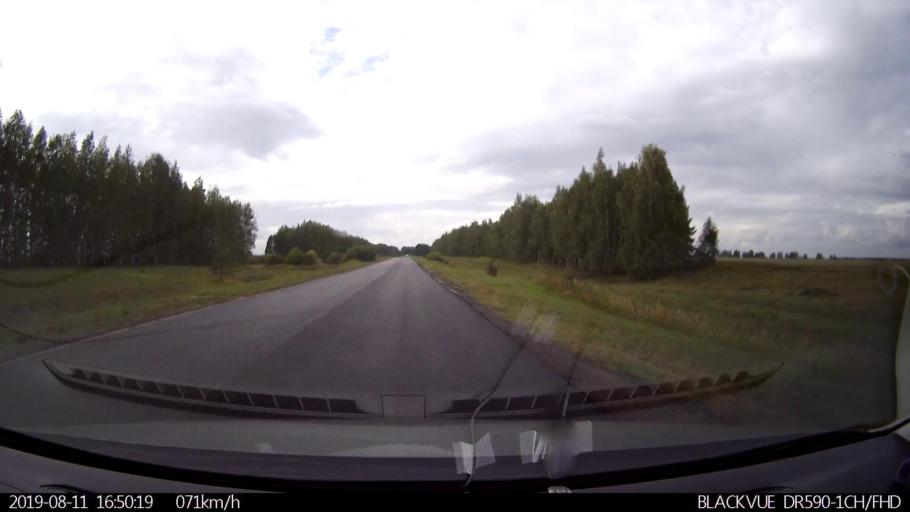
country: RU
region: Ulyanovsk
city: Mayna
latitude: 54.2277
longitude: 47.6888
